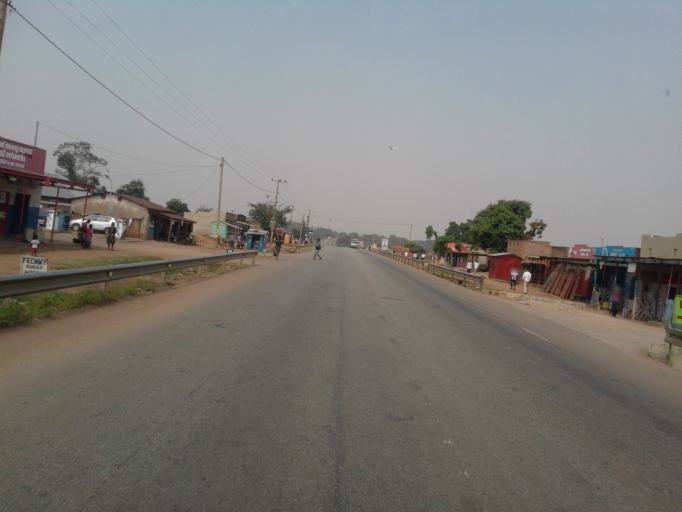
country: UG
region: Eastern Region
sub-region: Bugiri District
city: Bugiri
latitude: 0.6232
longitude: 33.6213
